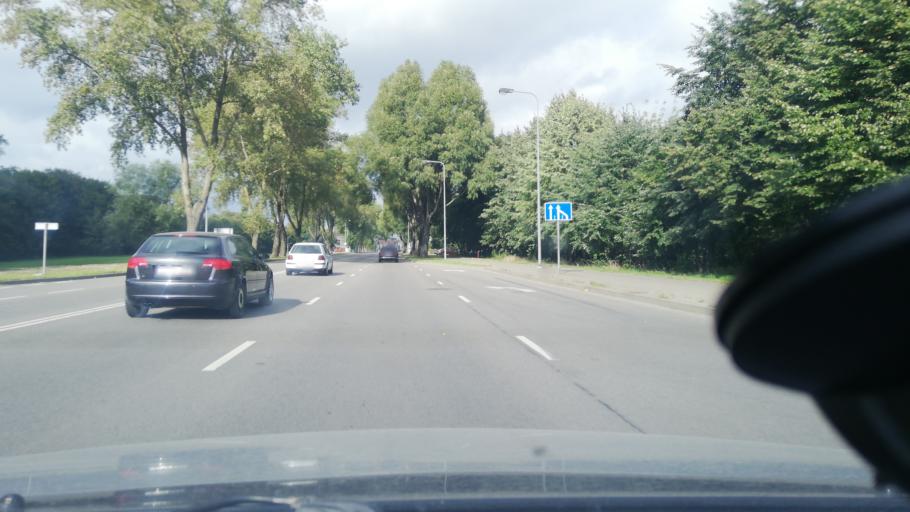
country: LT
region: Klaipedos apskritis
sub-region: Klaipeda
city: Klaipeda
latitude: 55.6715
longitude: 21.1581
